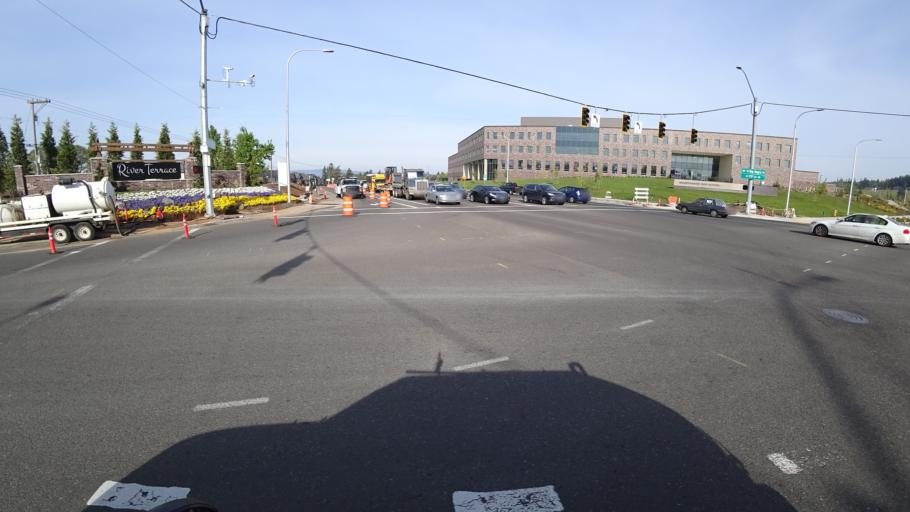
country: US
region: Oregon
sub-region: Washington County
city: King City
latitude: 45.4262
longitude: -122.8535
